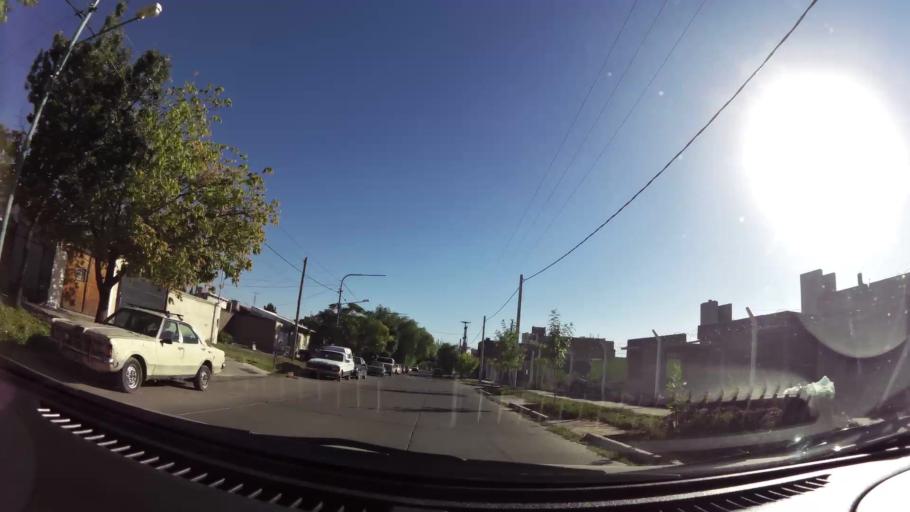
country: AR
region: Mendoza
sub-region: Departamento de Godoy Cruz
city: Godoy Cruz
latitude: -32.9347
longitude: -68.8319
